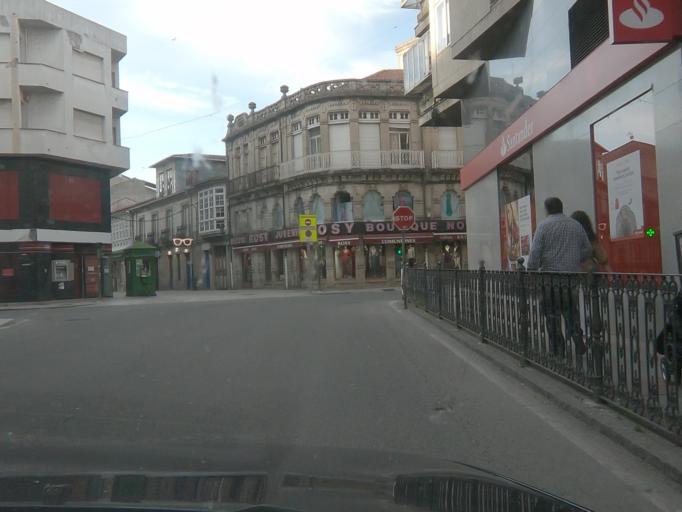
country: ES
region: Galicia
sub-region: Provincia de Ourense
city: Verin
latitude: 41.9400
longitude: -7.4376
